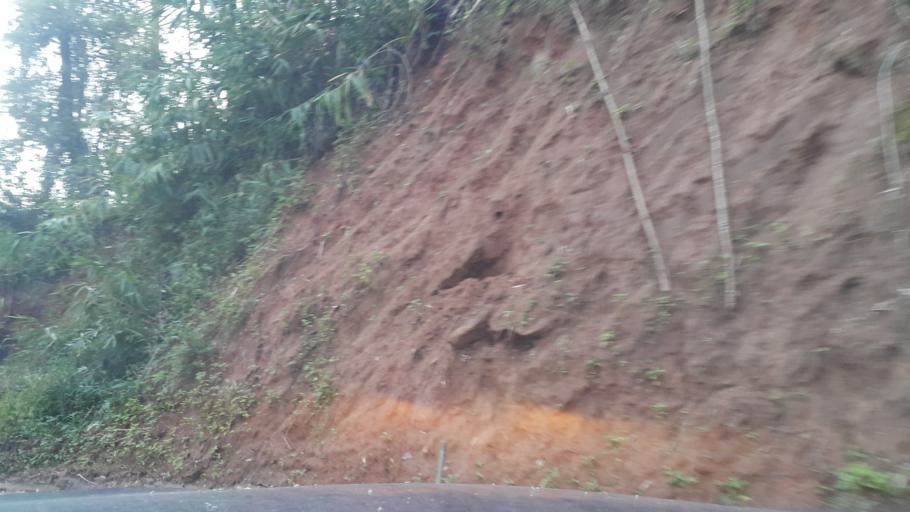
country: TH
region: Chiang Mai
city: Samoeng
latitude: 19.0065
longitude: 98.6698
